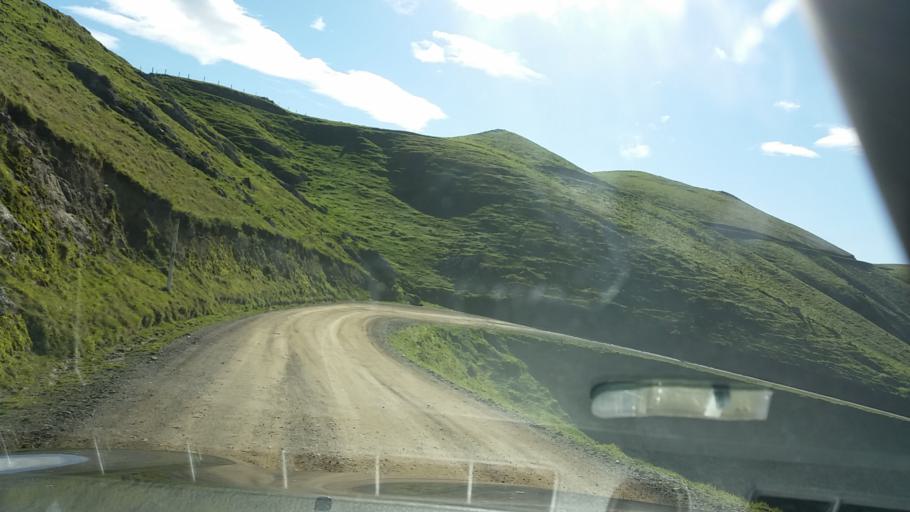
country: NZ
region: Marlborough
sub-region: Marlborough District
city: Picton
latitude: -40.9892
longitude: 173.8058
